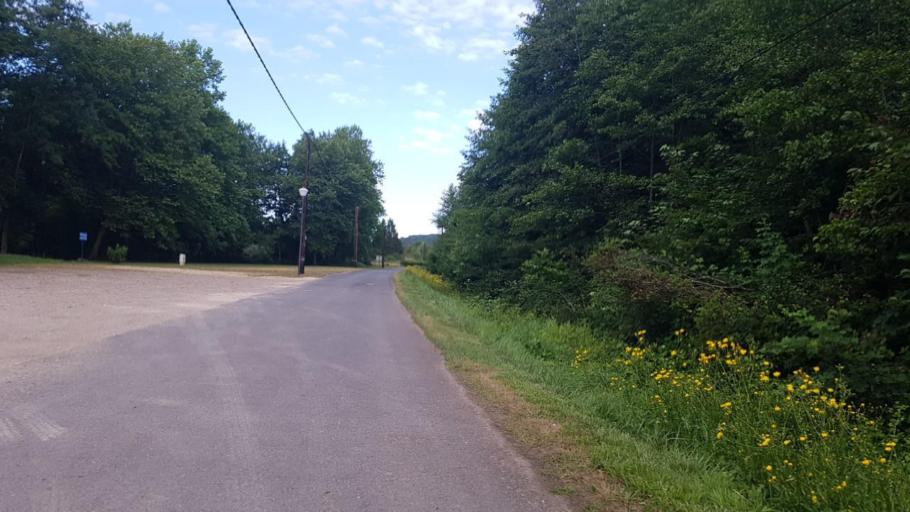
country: FR
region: Lorraine
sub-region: Departement de Meurthe-et-Moselle
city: Gondreville
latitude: 48.6534
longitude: 5.9914
